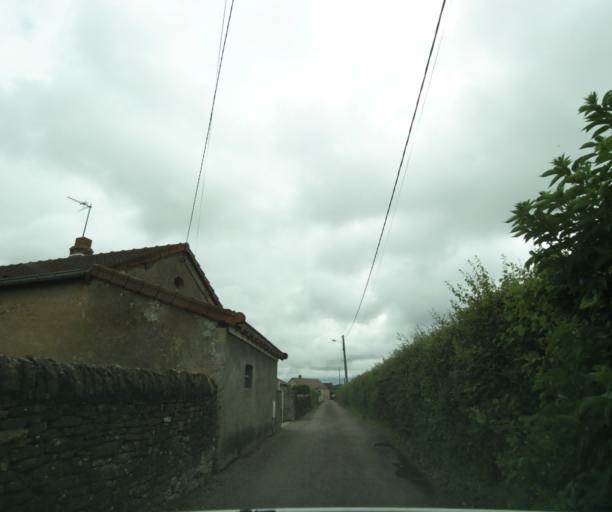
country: FR
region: Bourgogne
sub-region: Departement de Saone-et-Loire
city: Charolles
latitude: 46.4358
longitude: 4.2638
